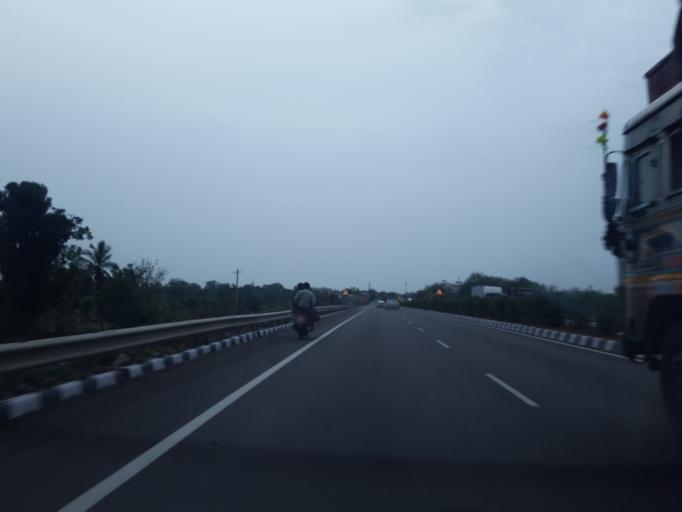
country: IN
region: Telangana
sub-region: Mahbubnagar
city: Farrukhnagar
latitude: 17.0762
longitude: 78.2269
